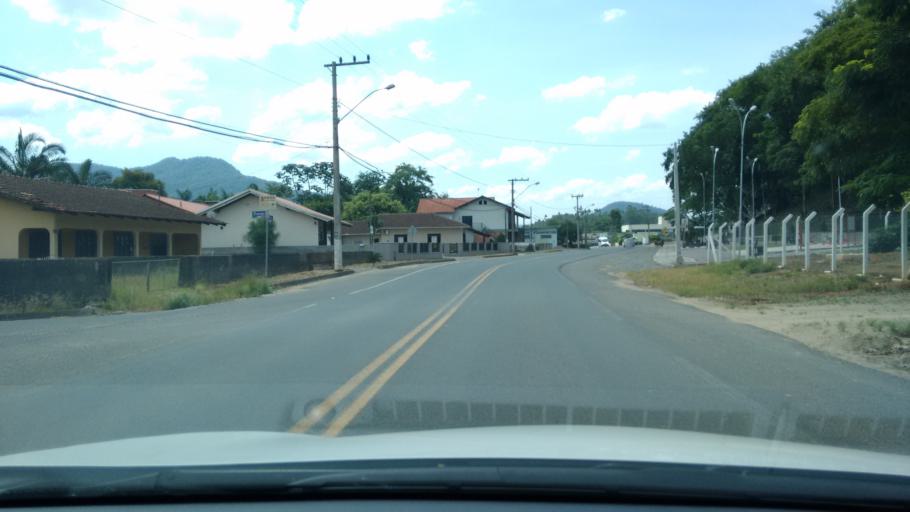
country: BR
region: Santa Catarina
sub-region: Timbo
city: Timbo
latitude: -26.8481
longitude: -49.3283
